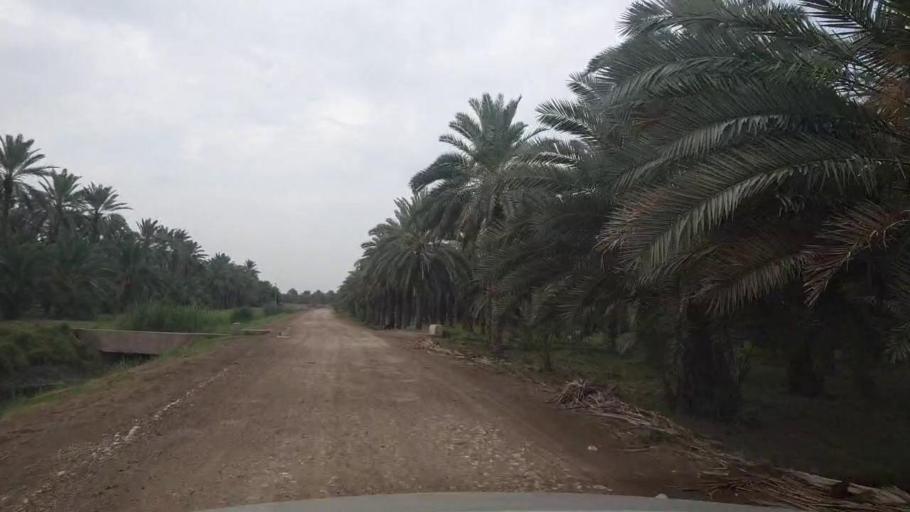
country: PK
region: Sindh
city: Sukkur
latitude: 27.6101
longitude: 68.8356
